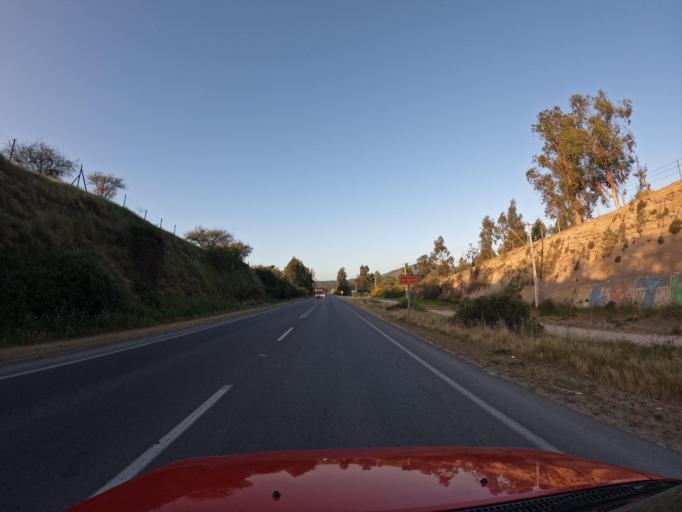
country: CL
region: O'Higgins
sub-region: Provincia de Cachapoal
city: San Vicente
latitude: -34.1532
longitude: -71.3860
